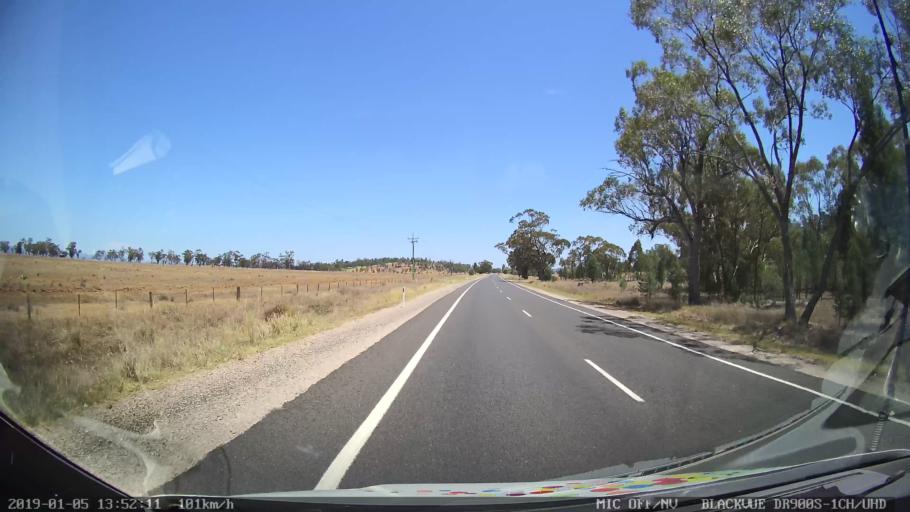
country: AU
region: New South Wales
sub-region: Gunnedah
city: Gunnedah
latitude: -31.0560
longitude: 150.2779
